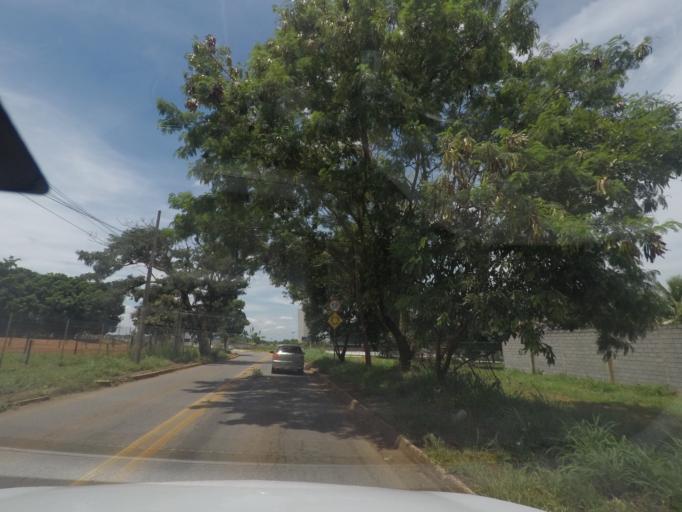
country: BR
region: Goias
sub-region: Goiania
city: Goiania
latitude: -16.6412
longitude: -49.2198
